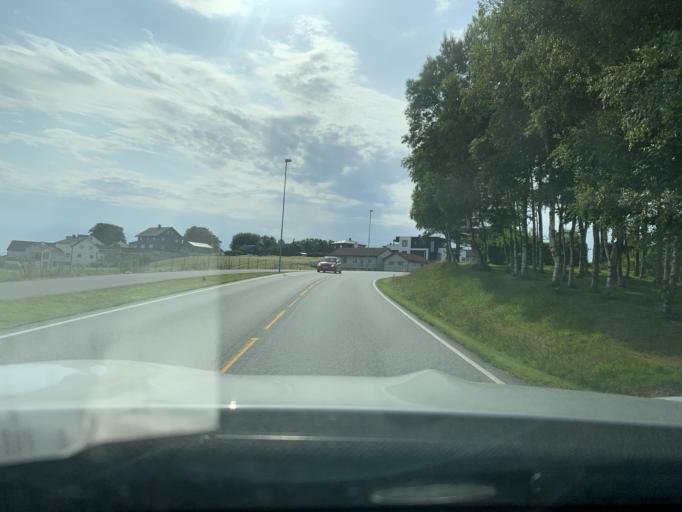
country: NO
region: Rogaland
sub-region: Time
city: Bryne
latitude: 58.7374
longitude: 5.6362
